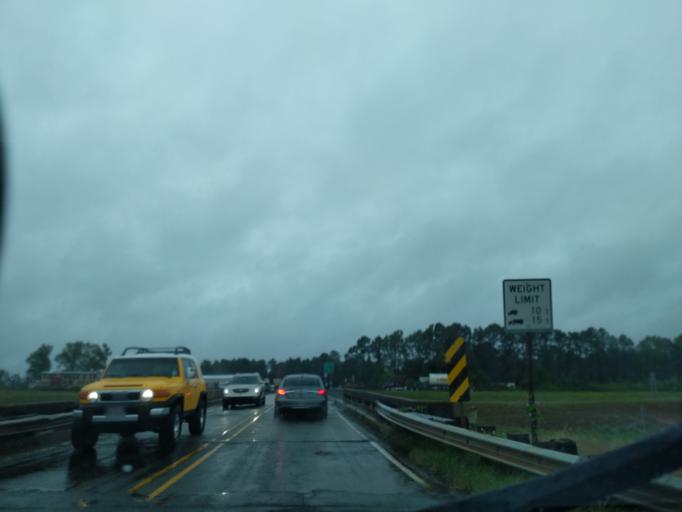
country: US
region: Louisiana
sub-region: Webster Parish
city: Minden
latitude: 32.5811
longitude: -93.2480
